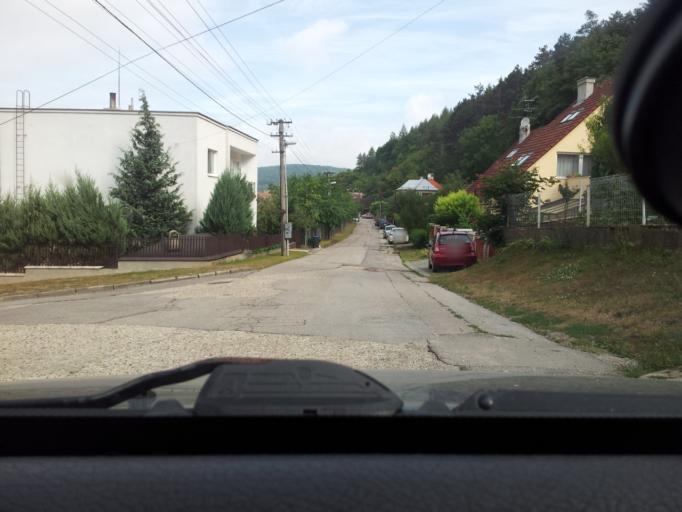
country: SK
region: Trenciansky
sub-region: Okres Trencin
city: Trencin
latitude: 48.8922
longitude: 18.0886
